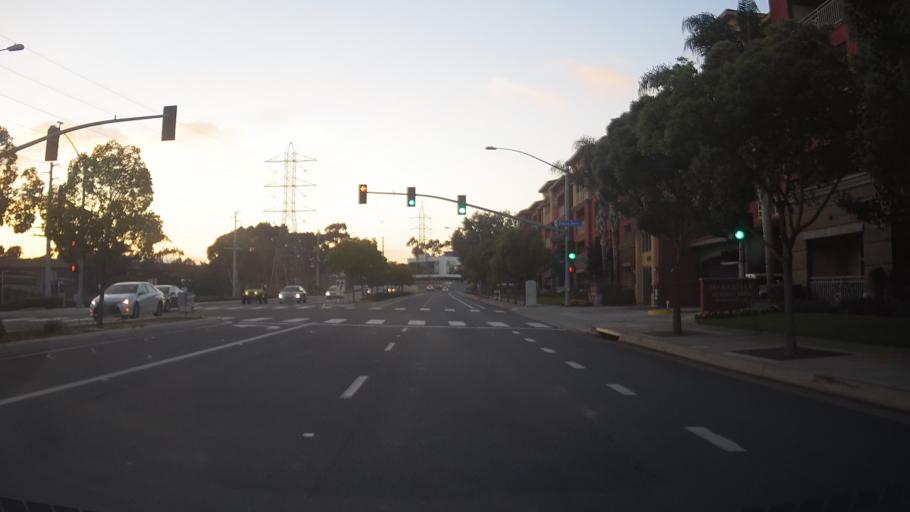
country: US
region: California
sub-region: San Diego County
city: San Diego
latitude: 32.8061
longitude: -117.1502
